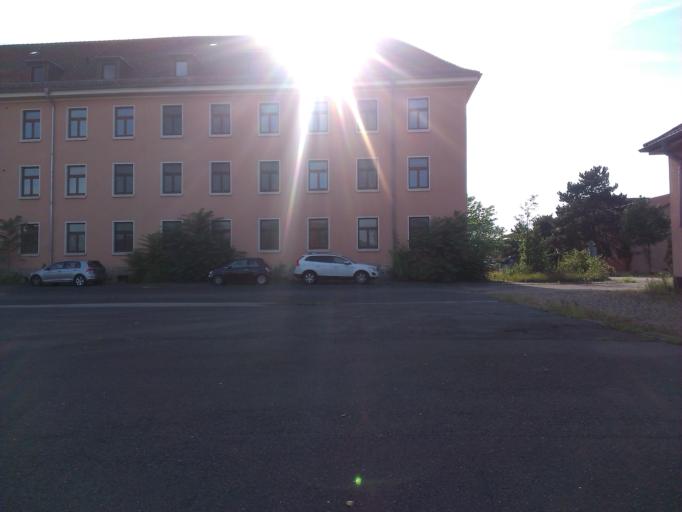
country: DE
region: Baden-Wuerttemberg
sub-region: Karlsruhe Region
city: Mannheim
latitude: 49.4959
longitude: 8.5231
